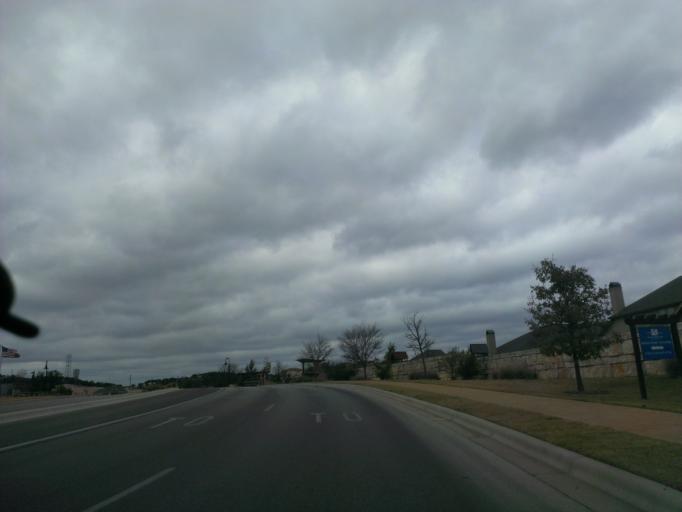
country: US
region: Texas
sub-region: Travis County
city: The Hills
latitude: 30.3507
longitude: -98.0093
